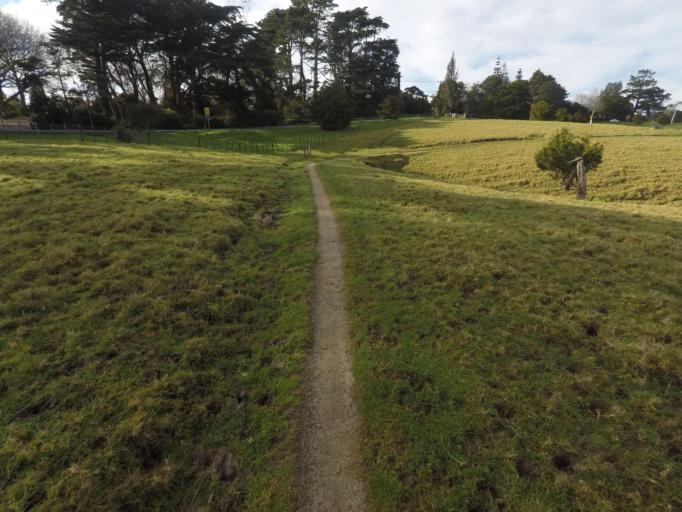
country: NZ
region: Auckland
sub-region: Auckland
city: Manukau City
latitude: -36.9909
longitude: 174.9163
